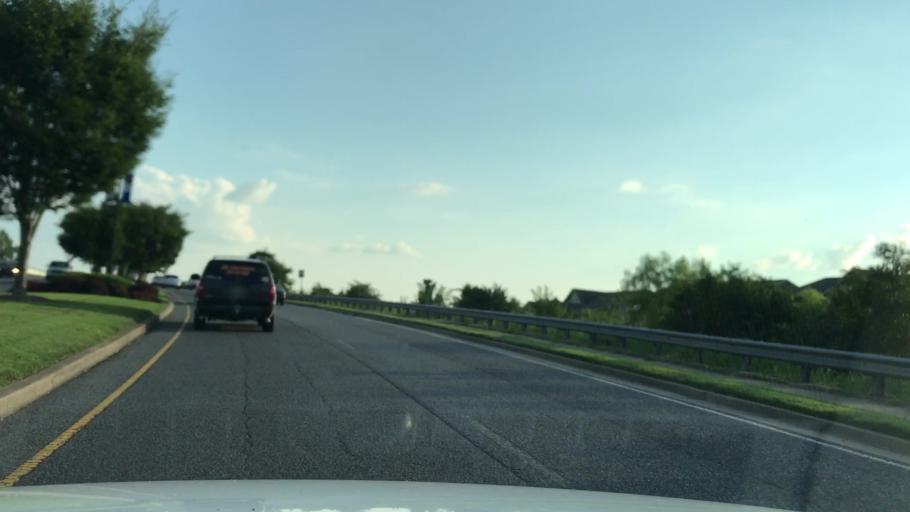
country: US
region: Tennessee
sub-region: Sumner County
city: Hendersonville
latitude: 36.3253
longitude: -86.5968
